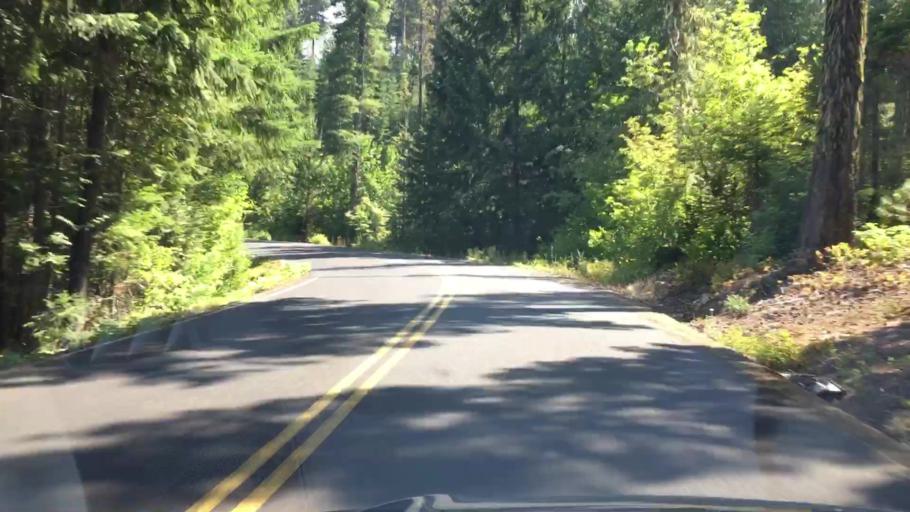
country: US
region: Washington
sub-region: Klickitat County
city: White Salmon
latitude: 46.0533
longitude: -121.5634
